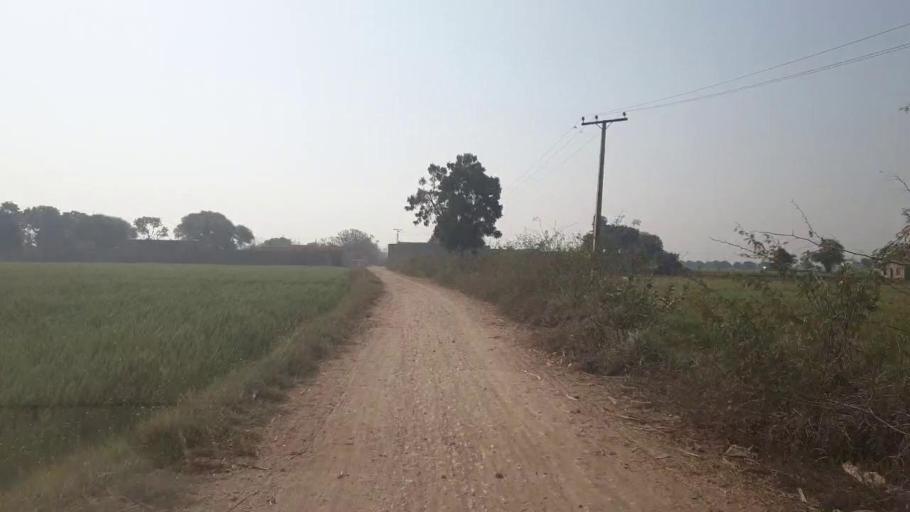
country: PK
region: Sindh
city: Tando Allahyar
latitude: 25.4603
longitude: 68.7820
